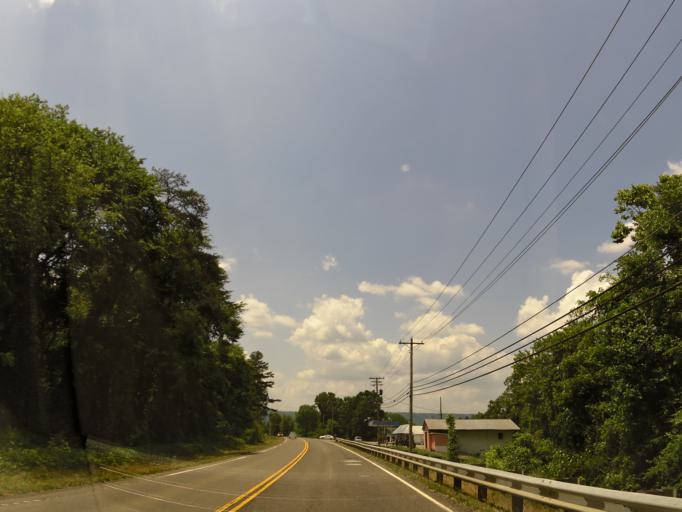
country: US
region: Tennessee
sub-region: Rhea County
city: Spring City
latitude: 35.6435
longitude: -84.8465
